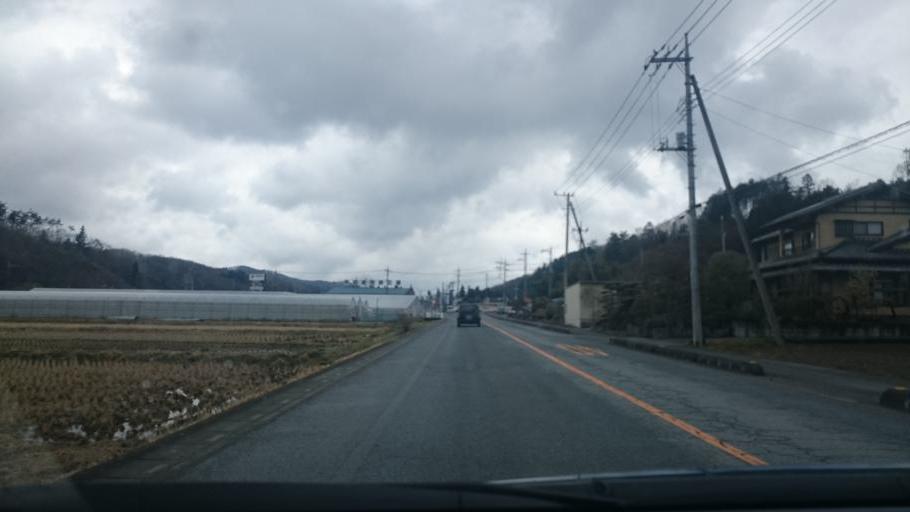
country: JP
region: Saitama
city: Chichibu
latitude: 36.0325
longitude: 139.0758
